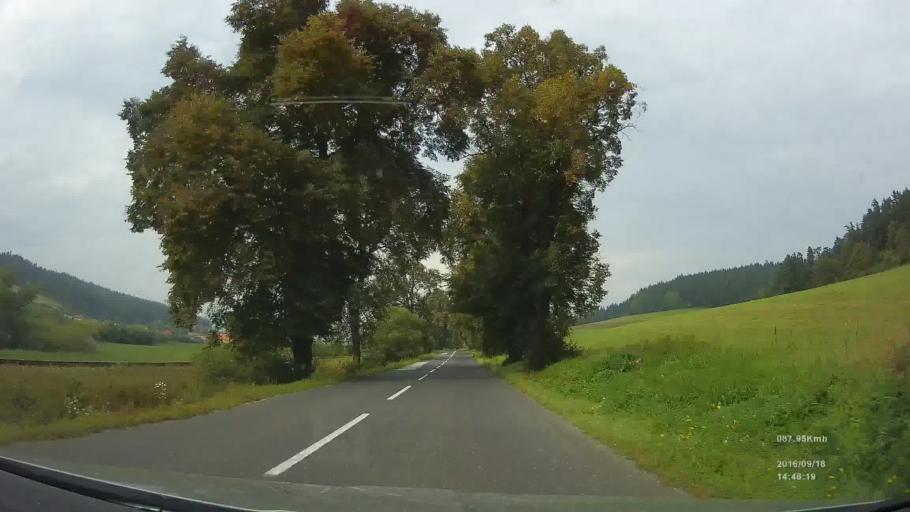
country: SK
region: Kosicky
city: Spisska Nova Ves
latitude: 48.9745
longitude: 20.5821
